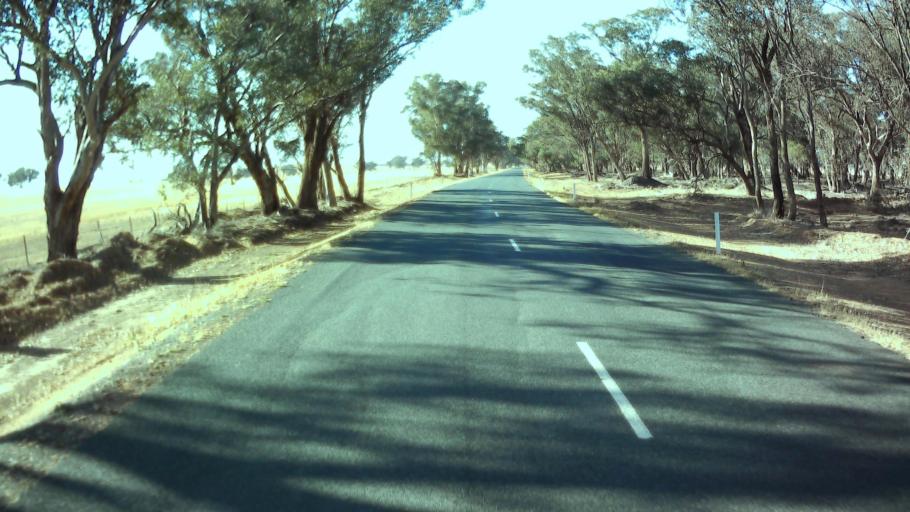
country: AU
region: New South Wales
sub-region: Weddin
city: Grenfell
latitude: -33.9513
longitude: 148.1385
